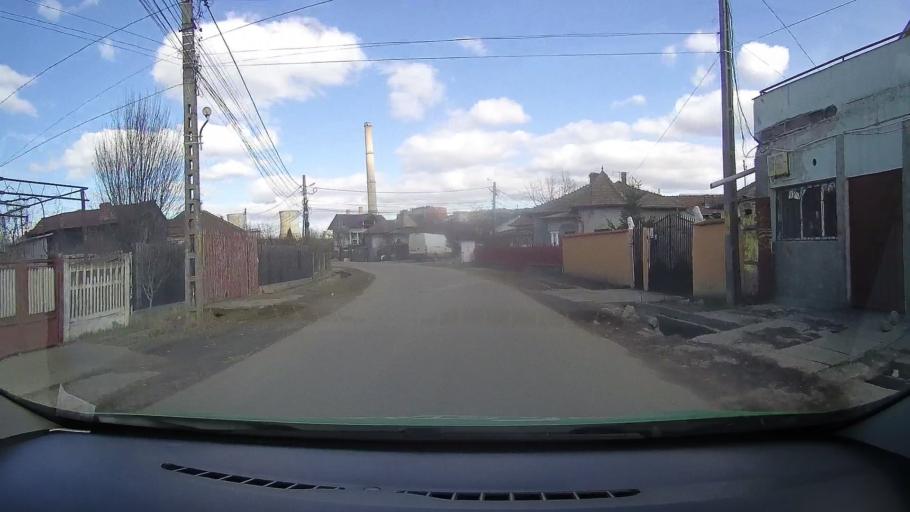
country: RO
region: Dambovita
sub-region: Comuna Doicesti
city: Doicesti
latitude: 44.9949
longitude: 25.3923
